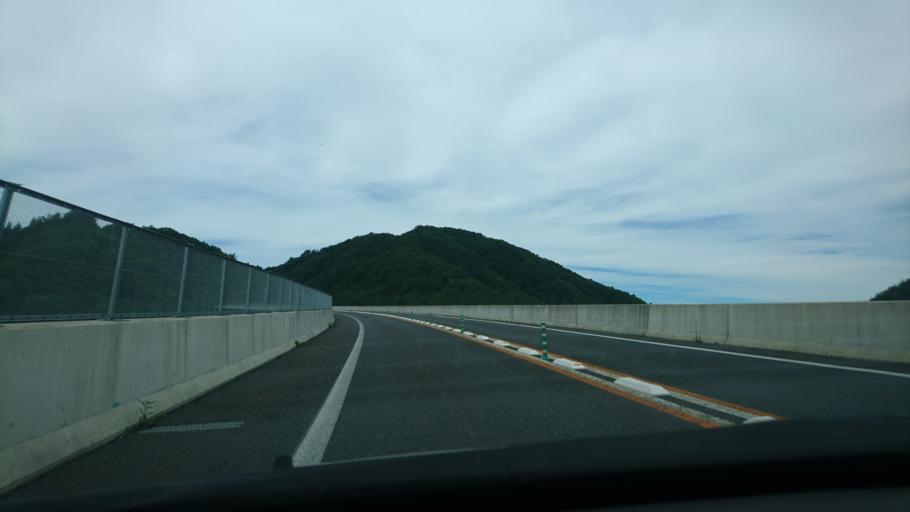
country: JP
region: Iwate
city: Miyako
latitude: 40.0076
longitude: 141.8895
